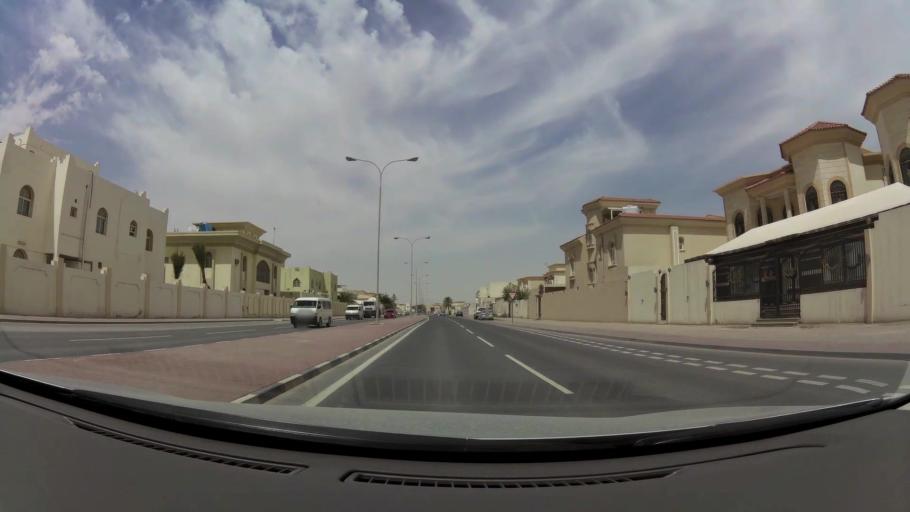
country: QA
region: Baladiyat ar Rayyan
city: Ar Rayyan
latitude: 25.2905
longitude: 51.4152
